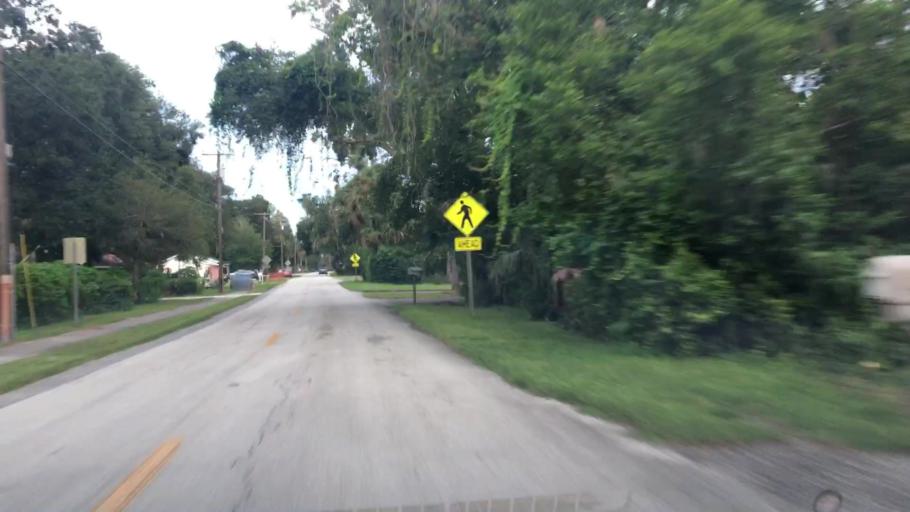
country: US
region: Florida
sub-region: Volusia County
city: DeBary
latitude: 28.8777
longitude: -81.3009
